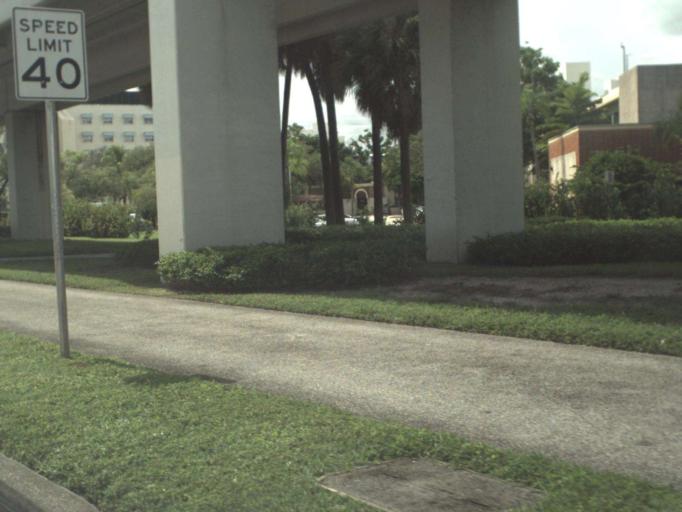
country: US
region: Florida
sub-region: Miami-Dade County
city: South Miami
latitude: 25.7031
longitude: -80.2913
